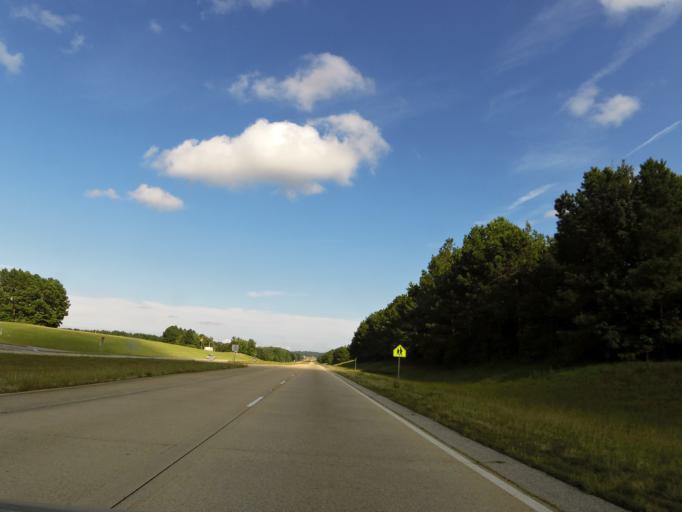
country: US
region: Mississippi
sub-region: Tishomingo County
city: Iuka
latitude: 34.8074
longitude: -88.2647
